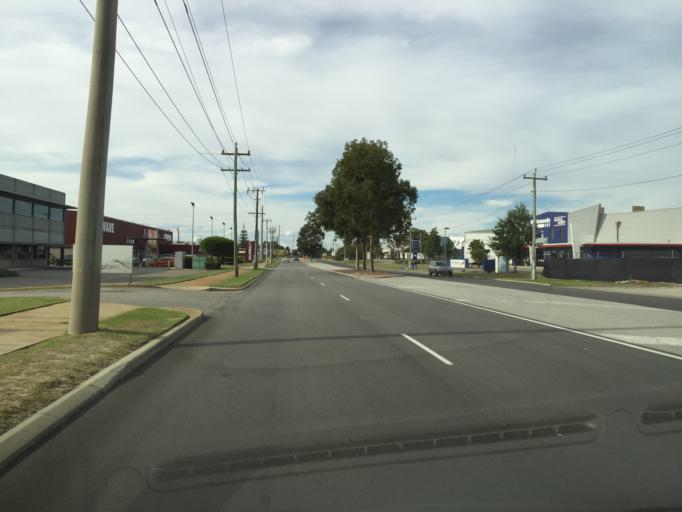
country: AU
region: Western Australia
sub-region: Canning
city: Canning Vale
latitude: -32.0628
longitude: 115.9038
